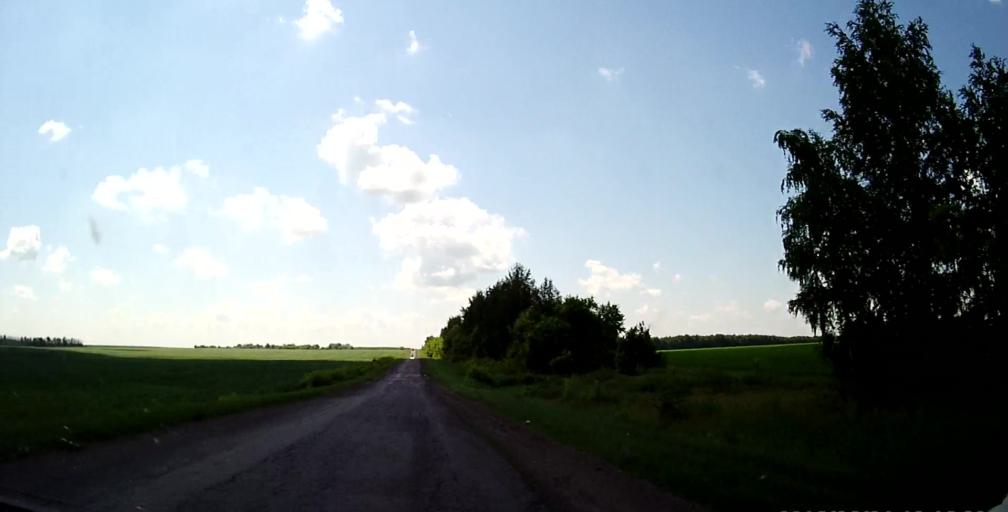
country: RU
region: Lipetsk
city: Chaplygin
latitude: 53.2842
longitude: 39.9603
